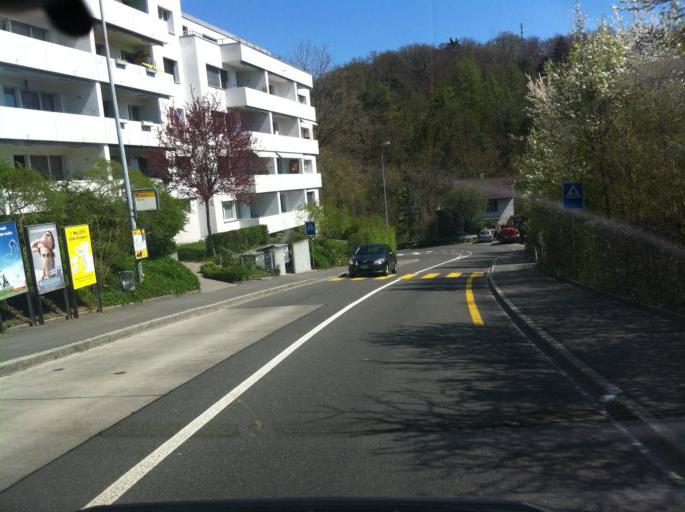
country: CH
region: Schaffhausen
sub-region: Bezirk Schaffhausen
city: Schaffhausen
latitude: 47.7122
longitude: 8.6300
